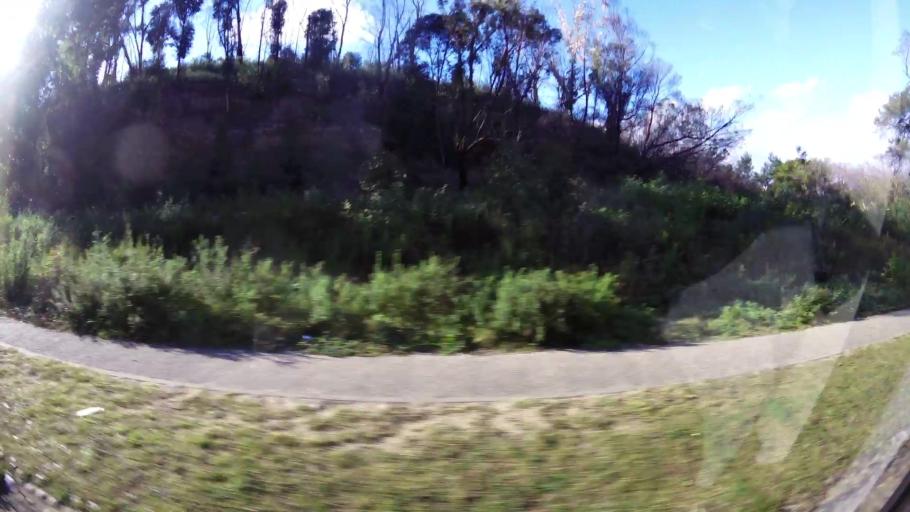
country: ZA
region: Western Cape
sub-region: Eden District Municipality
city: Knysna
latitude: -34.0316
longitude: 23.0471
